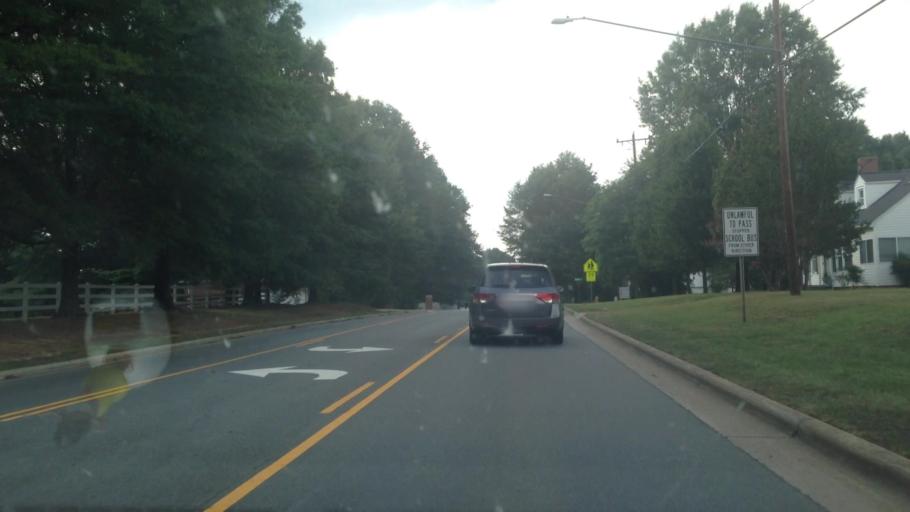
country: US
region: North Carolina
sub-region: Forsyth County
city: Kernersville
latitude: 36.1359
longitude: -80.1197
